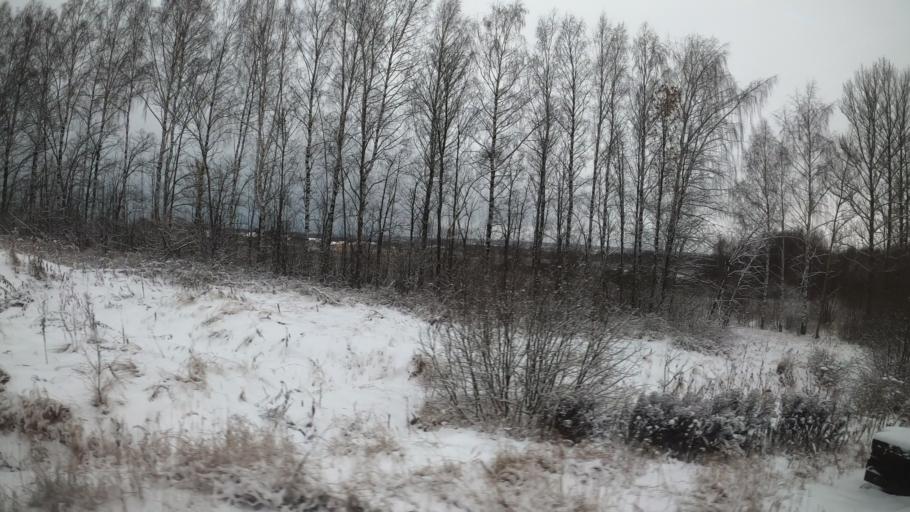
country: RU
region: Jaroslavl
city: Pereslavl'-Zalesskiy
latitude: 56.6876
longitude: 38.9185
